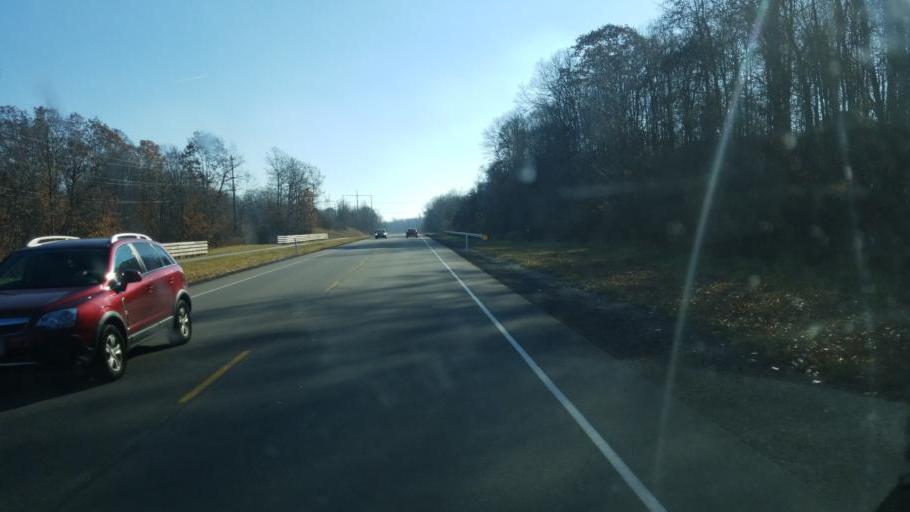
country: US
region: Ohio
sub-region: Geauga County
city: Chardon
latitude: 41.6009
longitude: -81.2313
